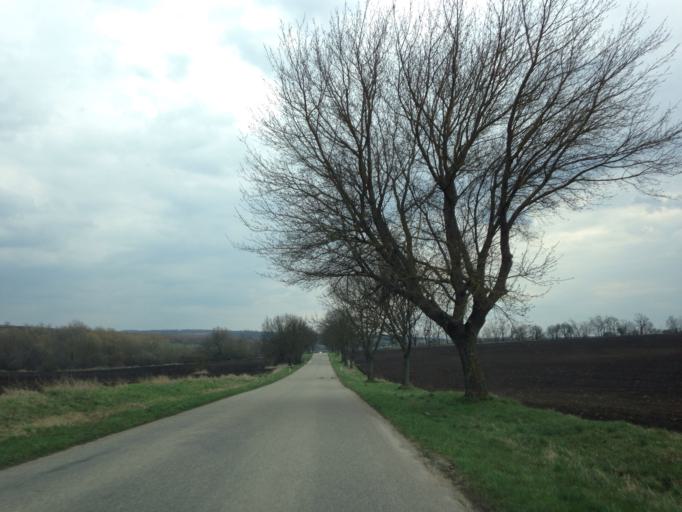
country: SK
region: Nitriansky
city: Svodin
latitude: 47.9800
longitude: 18.4033
